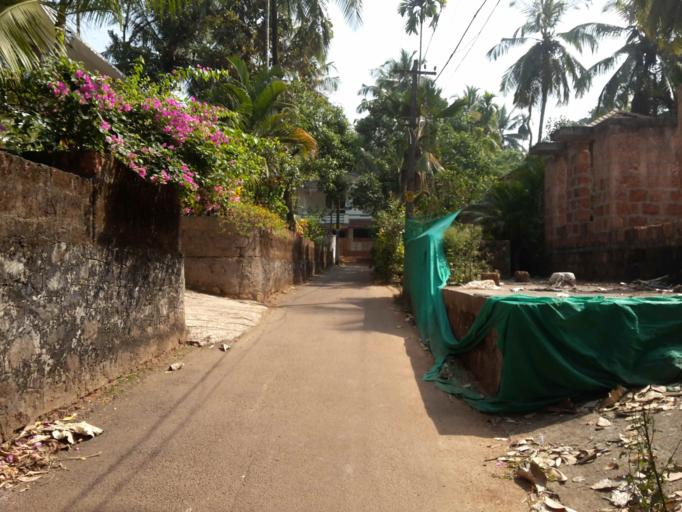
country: IN
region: Kerala
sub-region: Kozhikode
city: Kunnamangalam
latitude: 11.2962
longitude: 75.8386
